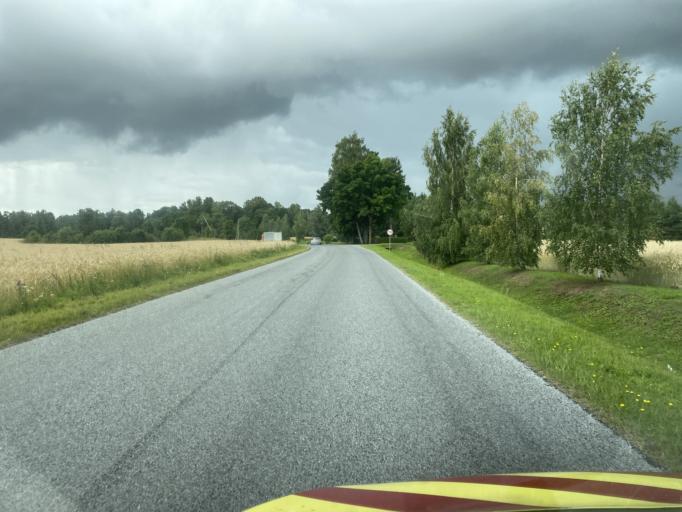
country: EE
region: Valgamaa
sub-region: Torva linn
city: Torva
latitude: 58.1505
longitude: 25.8063
